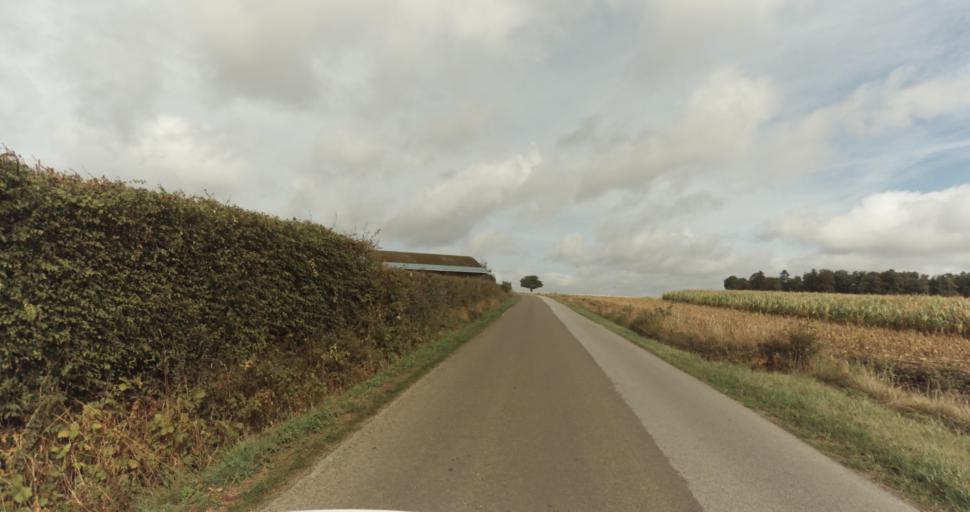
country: FR
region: Lower Normandy
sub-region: Departement de l'Orne
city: Gace
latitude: 48.8408
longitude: 0.3768
